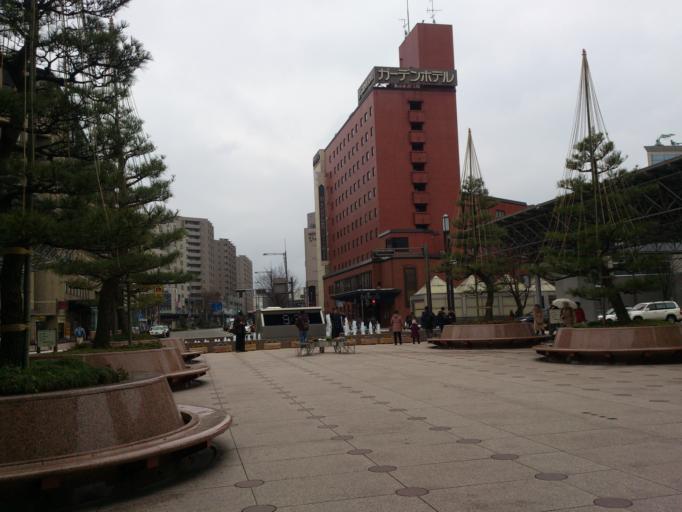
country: JP
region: Ishikawa
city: Kanazawa-shi
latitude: 36.5779
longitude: 136.6491
